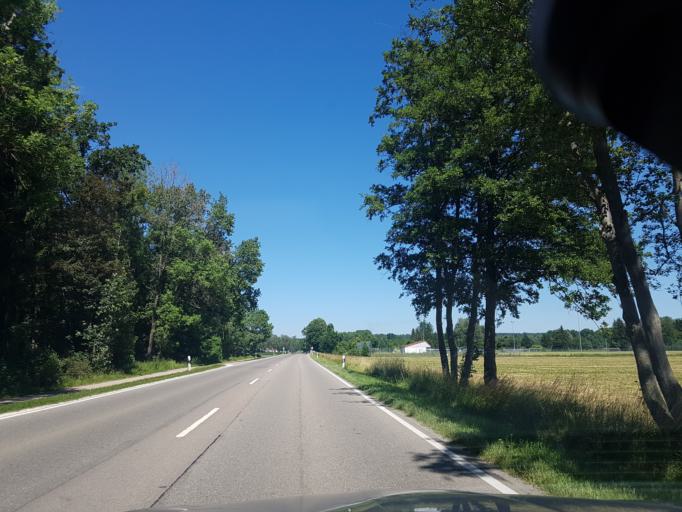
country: DE
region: Bavaria
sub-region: Swabia
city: Weissenhorn
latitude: 48.2978
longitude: 10.1458
